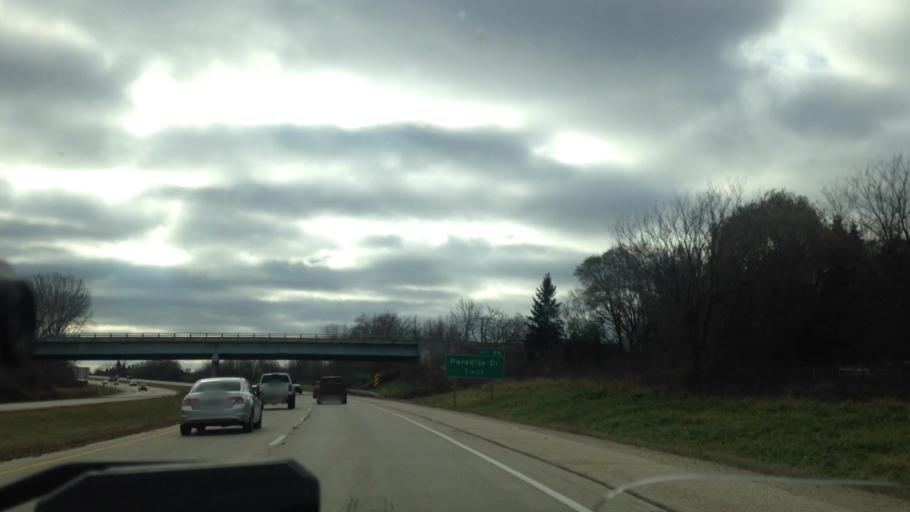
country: US
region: Wisconsin
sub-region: Washington County
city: West Bend
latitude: 43.4140
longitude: -88.2065
